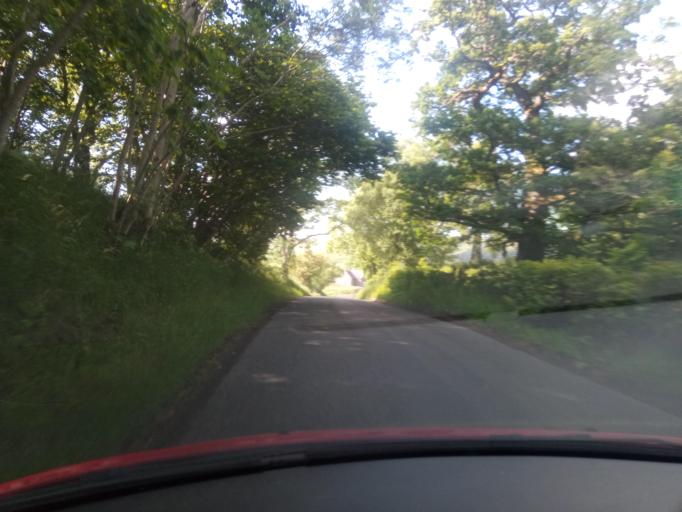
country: GB
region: Scotland
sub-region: The Scottish Borders
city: Innerleithen
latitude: 55.5013
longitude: -2.9830
